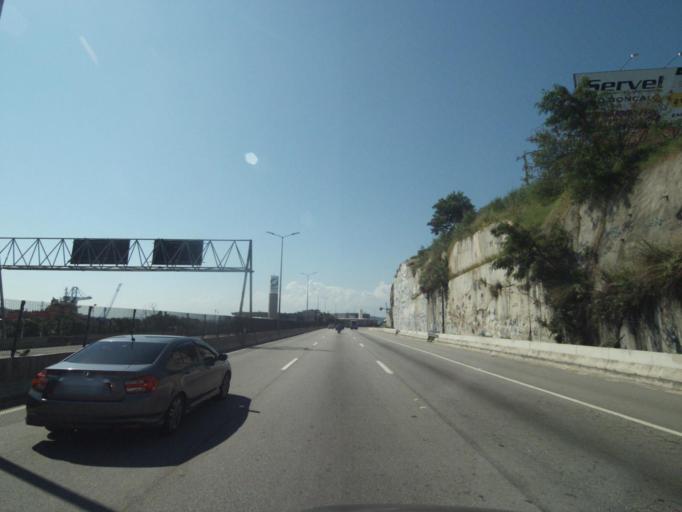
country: BR
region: Rio de Janeiro
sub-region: Niteroi
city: Niteroi
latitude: -22.8700
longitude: -43.1102
